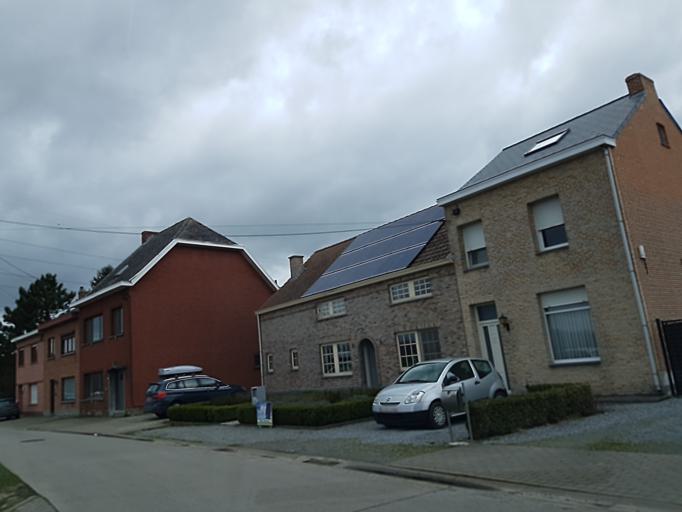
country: BE
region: Flanders
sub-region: Provincie Vlaams-Brabant
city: Kapelle-op-den-Bos
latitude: 51.0121
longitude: 4.4101
